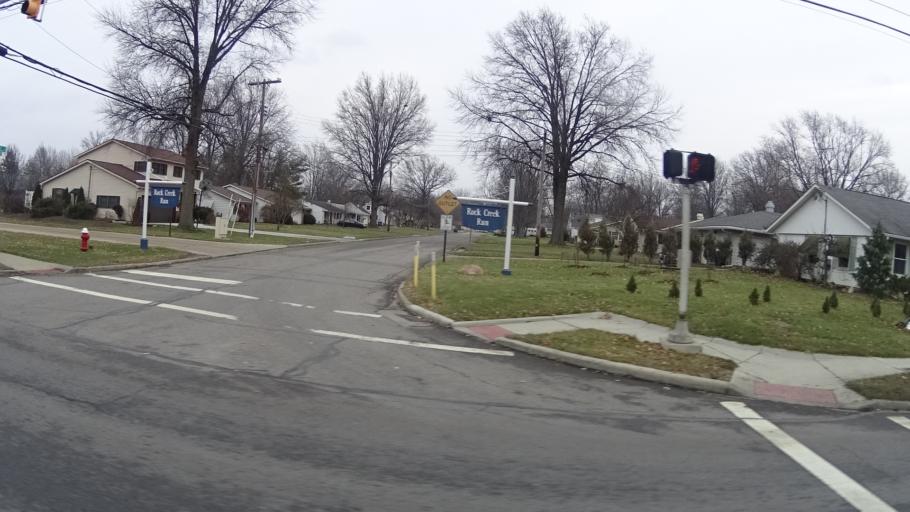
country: US
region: Ohio
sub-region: Lorain County
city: Amherst
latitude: 41.4119
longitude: -82.2091
